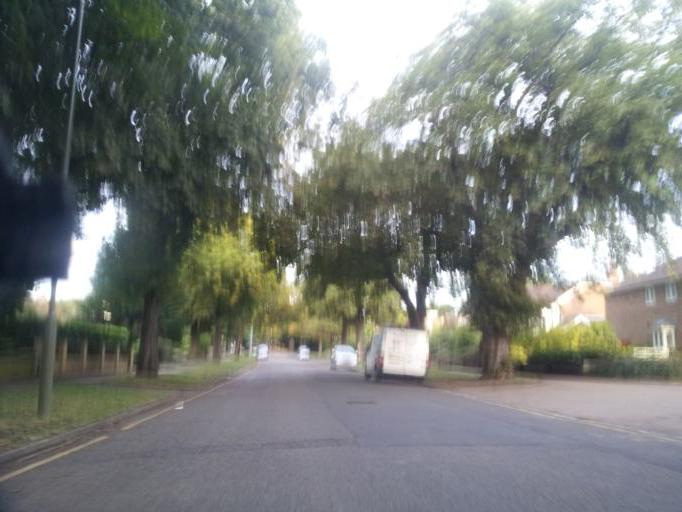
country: GB
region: England
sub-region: Greater London
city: Beckenham
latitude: 51.4140
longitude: -0.0276
